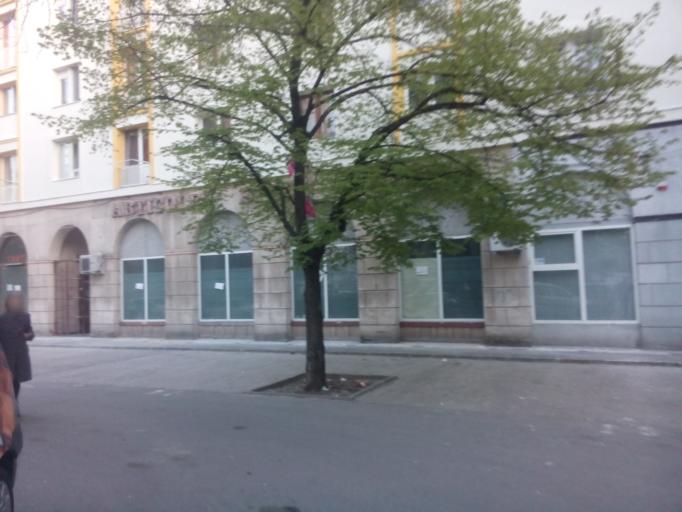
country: RO
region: Ilfov
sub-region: Comuna Fundeni-Dobroesti
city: Fundeni
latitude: 44.4329
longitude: 26.1527
